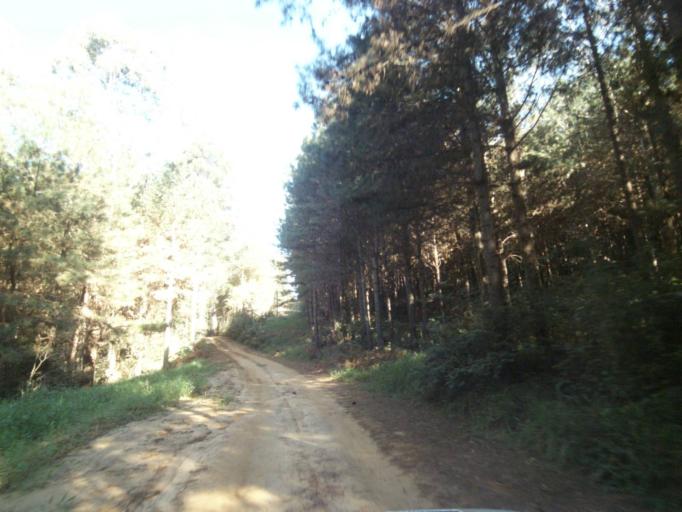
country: BR
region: Parana
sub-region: Tibagi
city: Tibagi
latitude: -24.5538
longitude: -50.4726
